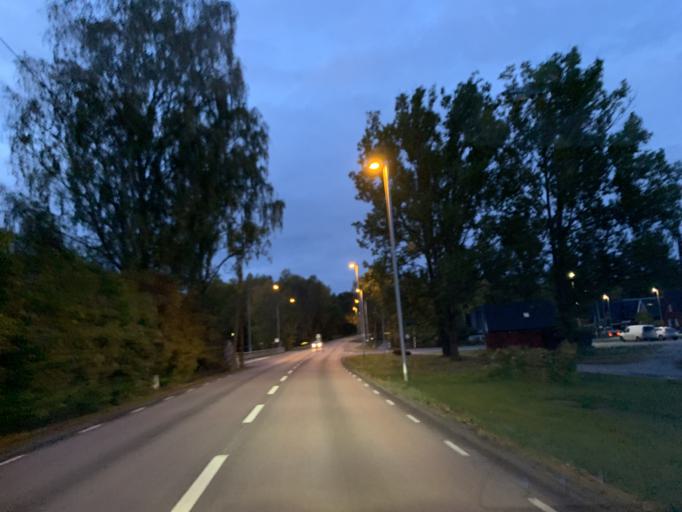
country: SE
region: Stockholm
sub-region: Botkyrka Kommun
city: Varsta
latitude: 59.1697
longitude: 17.7977
